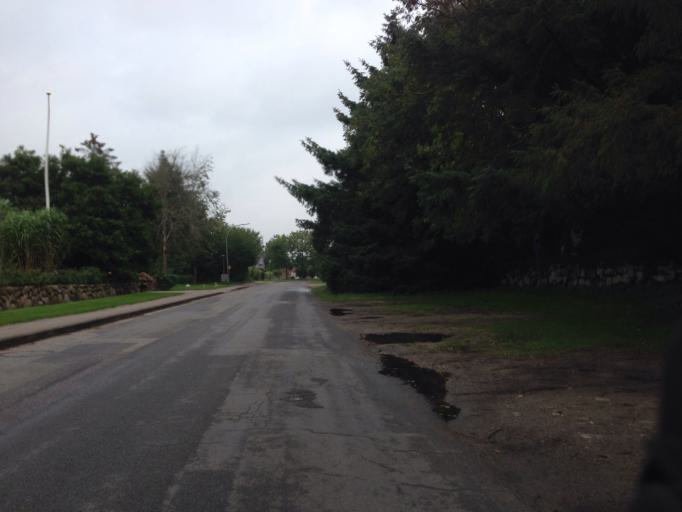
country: DE
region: Schleswig-Holstein
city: Wrixum
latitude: 54.6955
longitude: 8.5494
